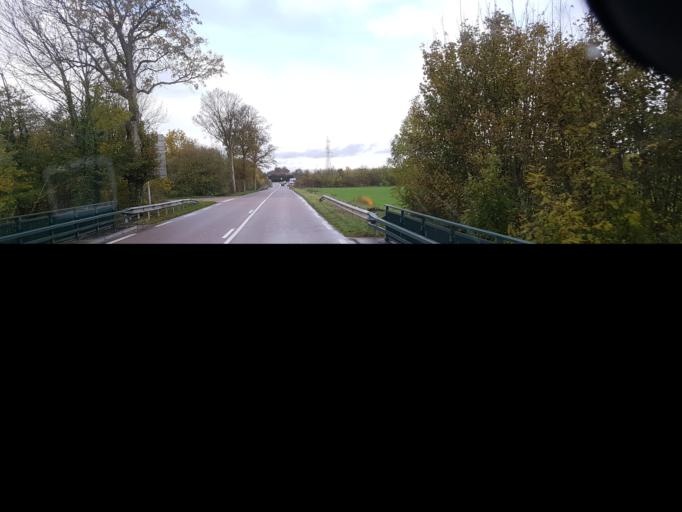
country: FR
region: Champagne-Ardenne
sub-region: Departement de l'Aube
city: Saint-Parres-aux-Tertres
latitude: 48.2852
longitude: 4.1679
